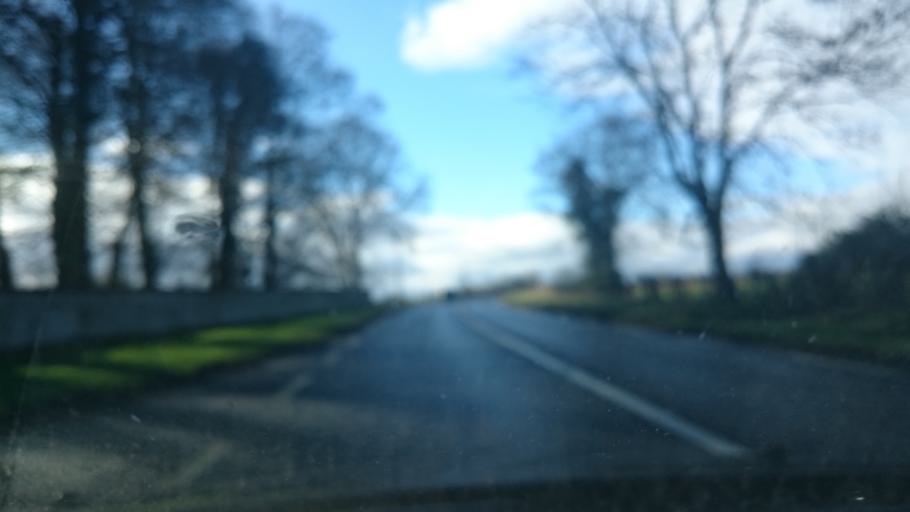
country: IE
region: Leinster
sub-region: Kilkenny
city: Callan
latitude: 52.5831
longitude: -7.3147
